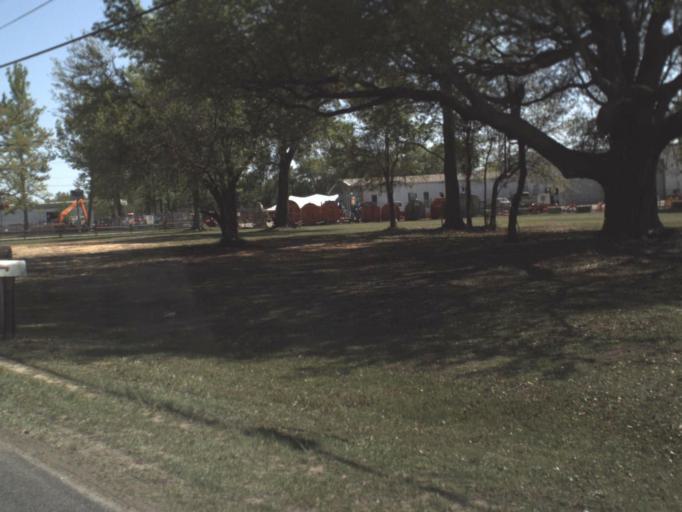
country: US
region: Florida
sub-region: Escambia County
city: Bellview
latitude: 30.4803
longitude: -87.3104
